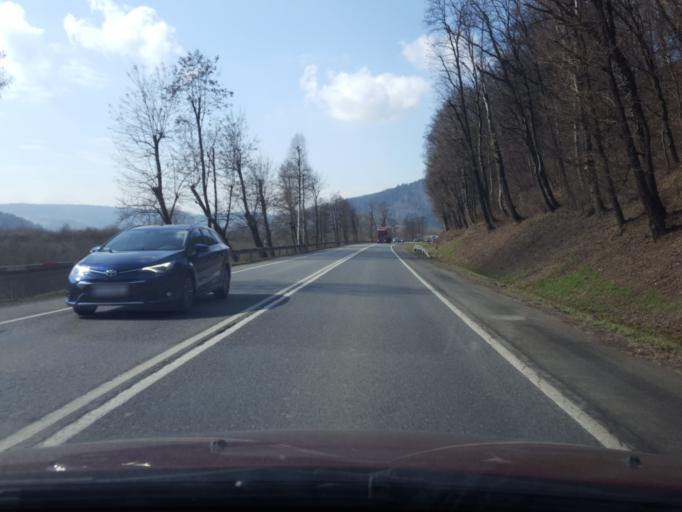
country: PL
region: Lesser Poland Voivodeship
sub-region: Powiat nowosadecki
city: Lososina Dolna
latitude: 49.6951
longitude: 20.6594
